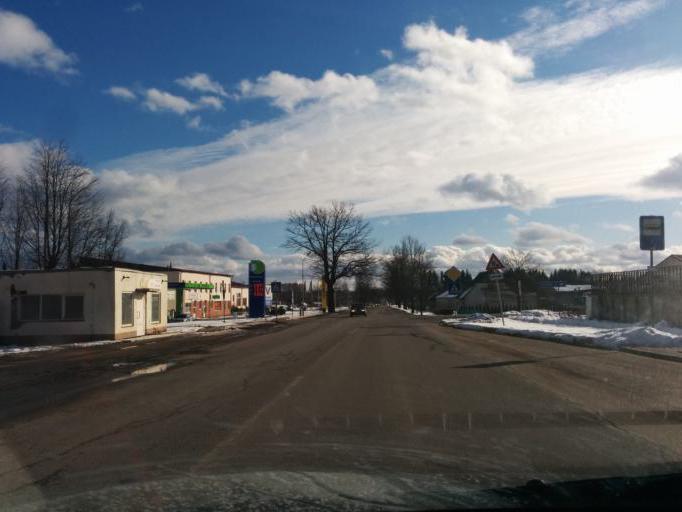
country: LV
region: Gulbenes Rajons
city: Gulbene
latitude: 57.1757
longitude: 26.7451
